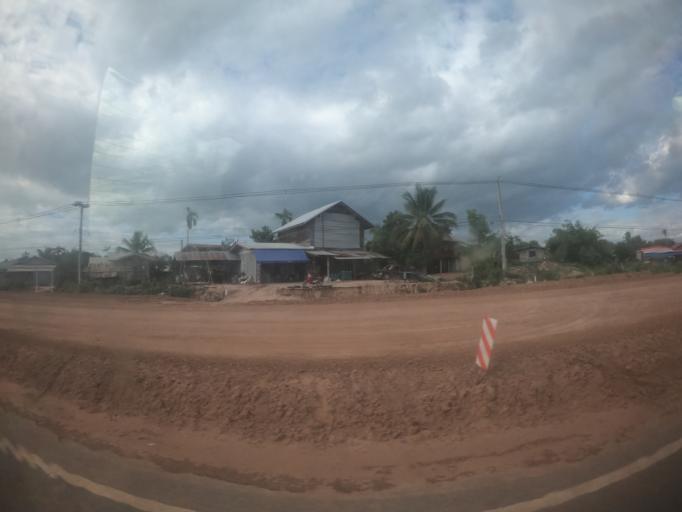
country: TH
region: Surin
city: Kap Choeng
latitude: 14.5074
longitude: 103.5561
